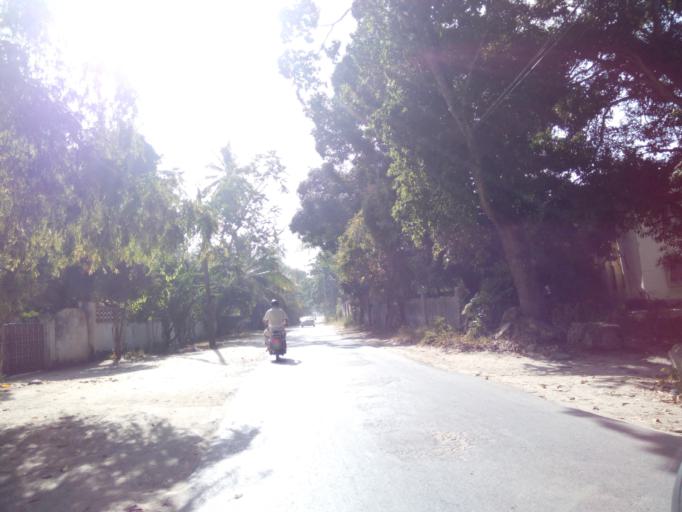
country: TZ
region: Zanzibar Urban/West
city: Zanzibar
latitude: -6.1726
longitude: 39.2011
